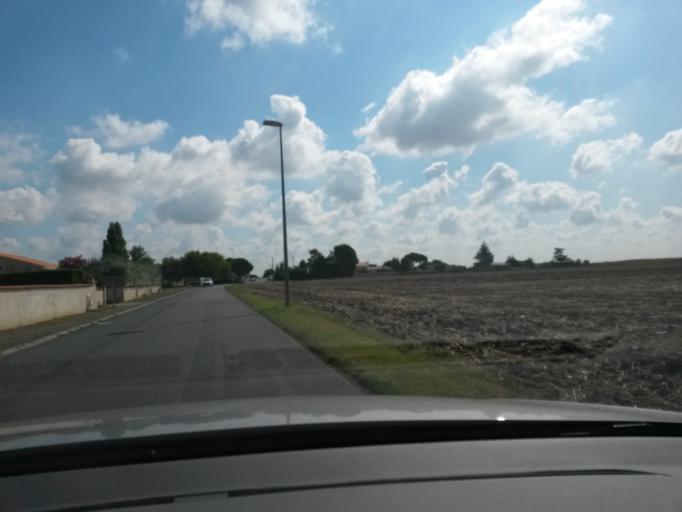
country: FR
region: Poitou-Charentes
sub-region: Departement de la Charente-Maritime
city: Port-des-Barques
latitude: 45.9410
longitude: -1.0698
